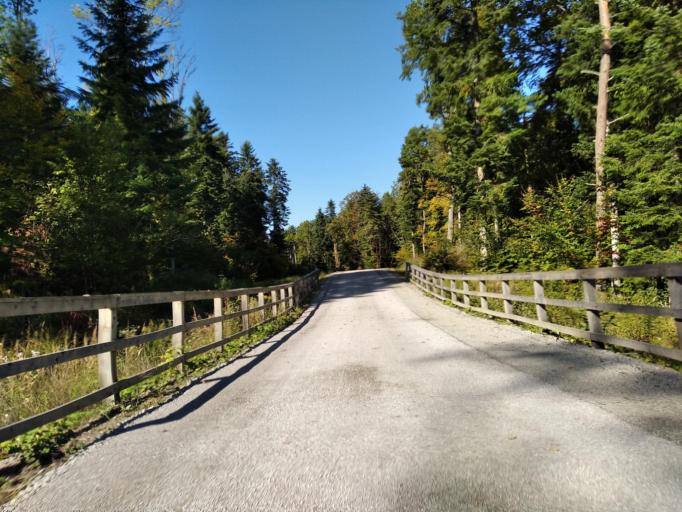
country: PL
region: Subcarpathian Voivodeship
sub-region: Powiat strzyzowski
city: Strzyzow
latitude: 49.8204
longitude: 21.8049
